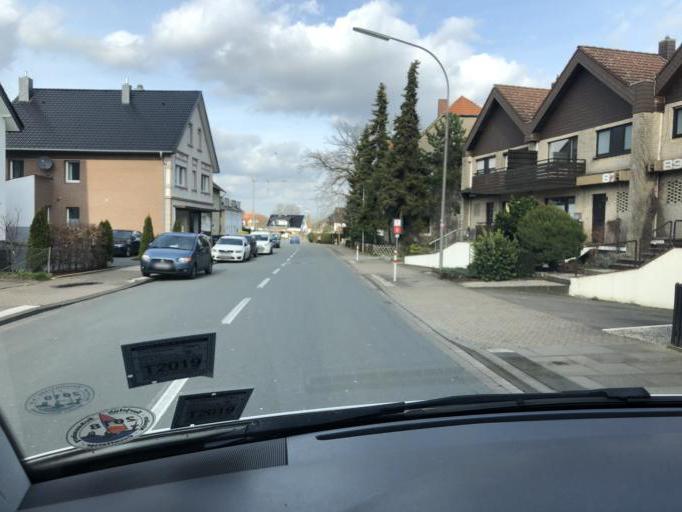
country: DE
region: North Rhine-Westphalia
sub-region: Regierungsbezirk Detmold
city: Herford
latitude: 52.1001
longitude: 8.6733
